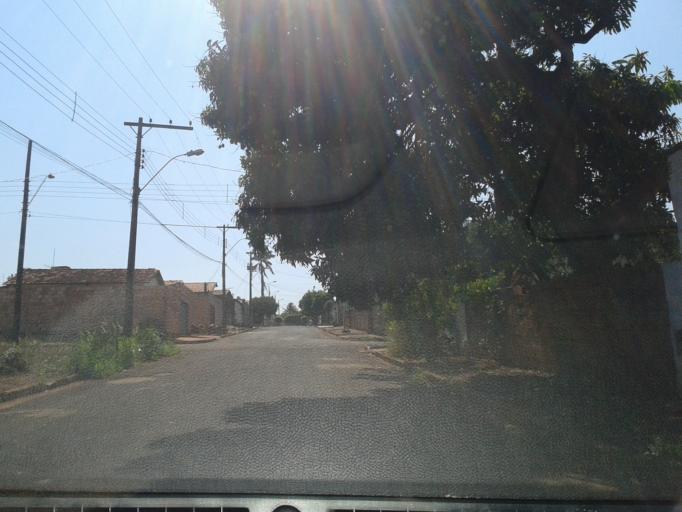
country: BR
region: Minas Gerais
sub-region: Ituiutaba
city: Ituiutaba
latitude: -18.9551
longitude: -49.4519
